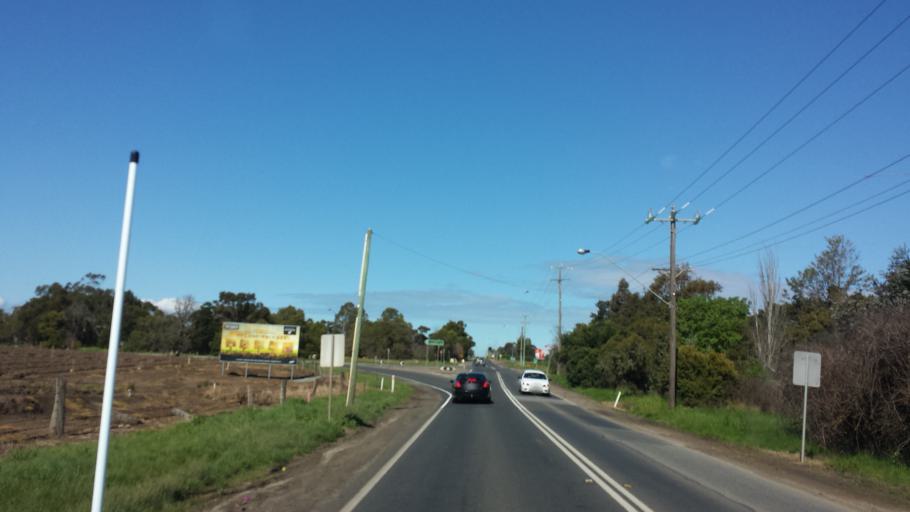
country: AU
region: Victoria
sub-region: Casey
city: Cranbourne East
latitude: -38.1260
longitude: 145.3257
